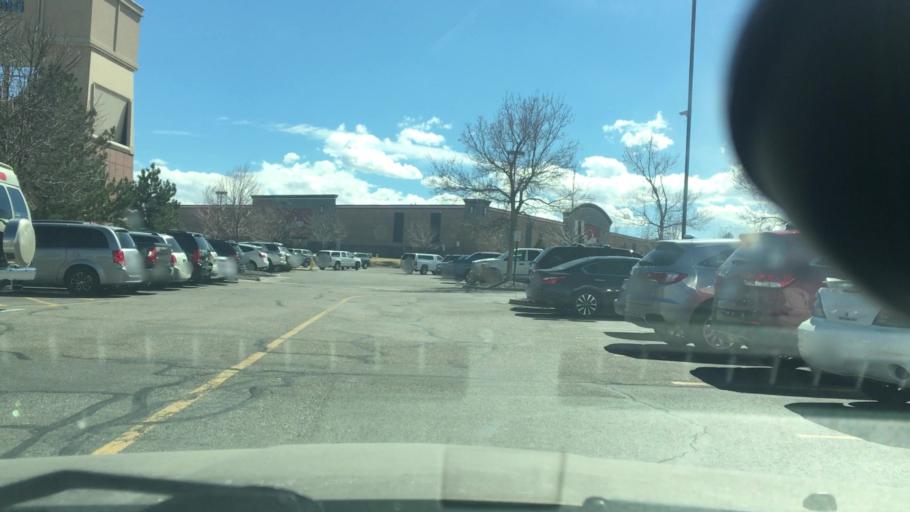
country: US
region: Colorado
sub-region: Adams County
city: Lone Tree
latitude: 39.5544
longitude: -104.8835
